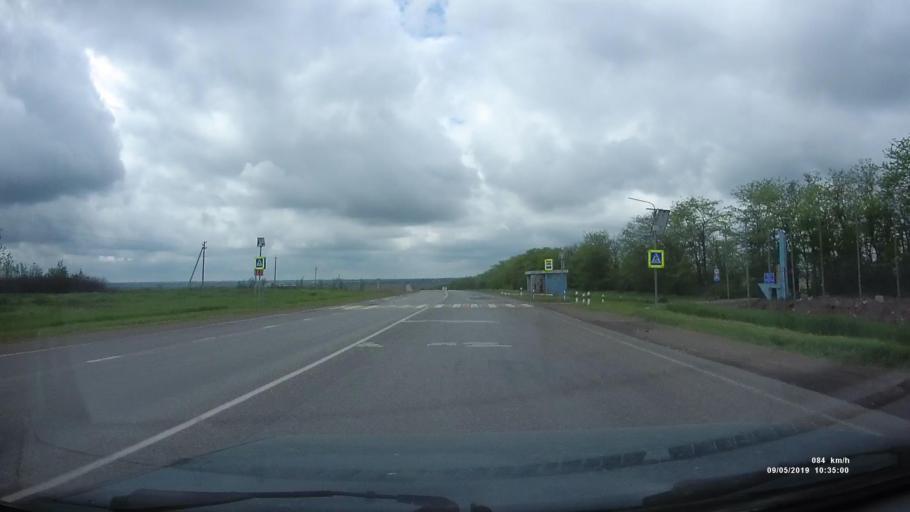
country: RU
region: Rostov
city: Peshkovo
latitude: 47.0478
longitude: 39.4158
